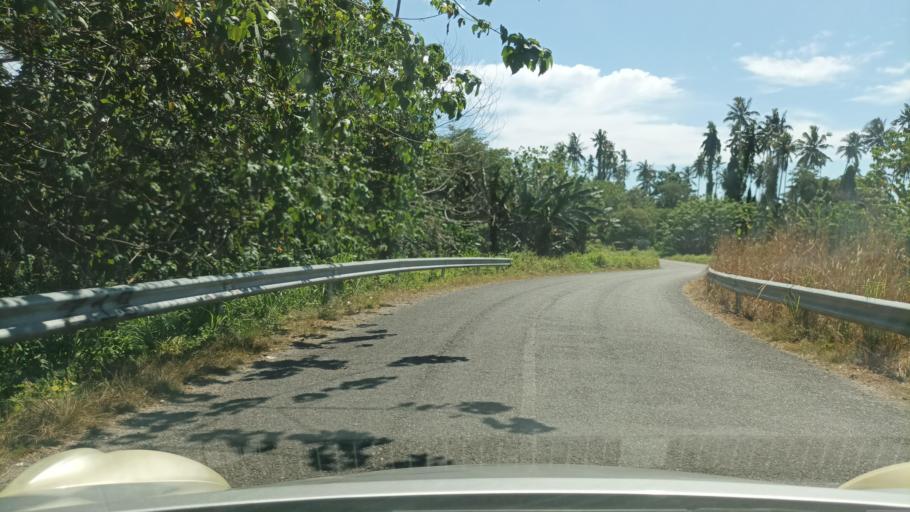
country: SB
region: Guadalcanal
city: Honiara
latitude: -9.3434
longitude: 159.8241
